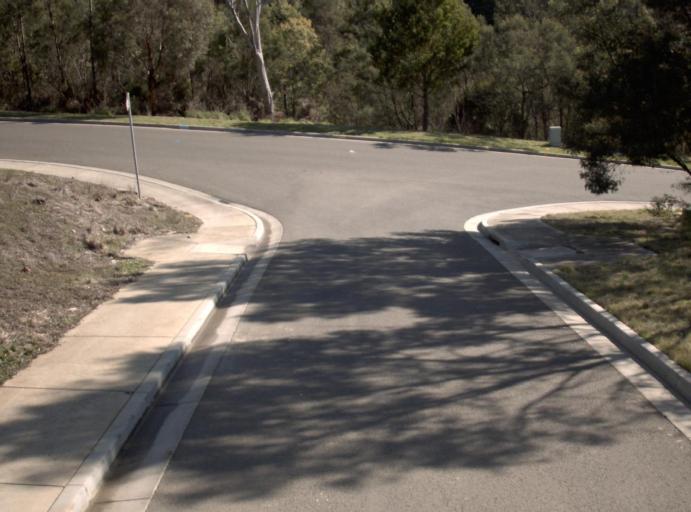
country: AU
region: Tasmania
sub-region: Launceston
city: Summerhill
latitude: -41.4743
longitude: 147.1549
